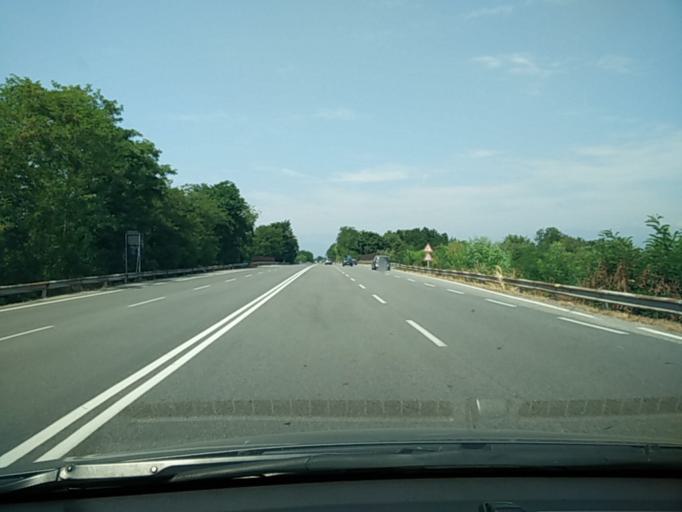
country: IT
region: Piedmont
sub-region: Provincia di Torino
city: Volpiano
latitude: 45.1856
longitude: 7.7842
